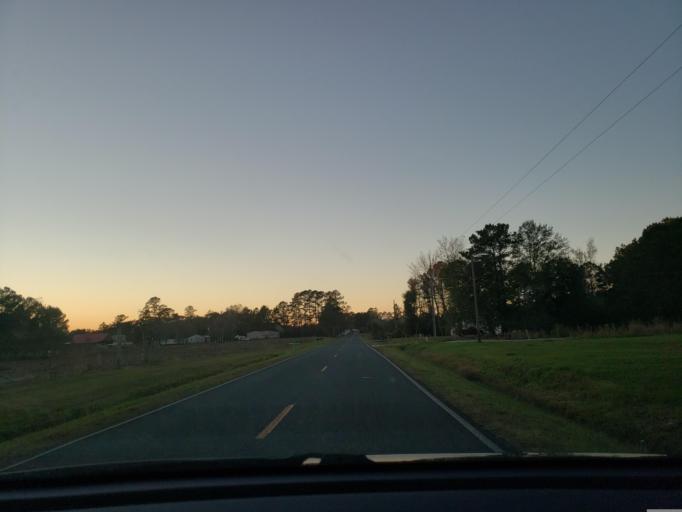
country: US
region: North Carolina
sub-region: Onslow County
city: Richlands
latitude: 34.7399
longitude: -77.6320
